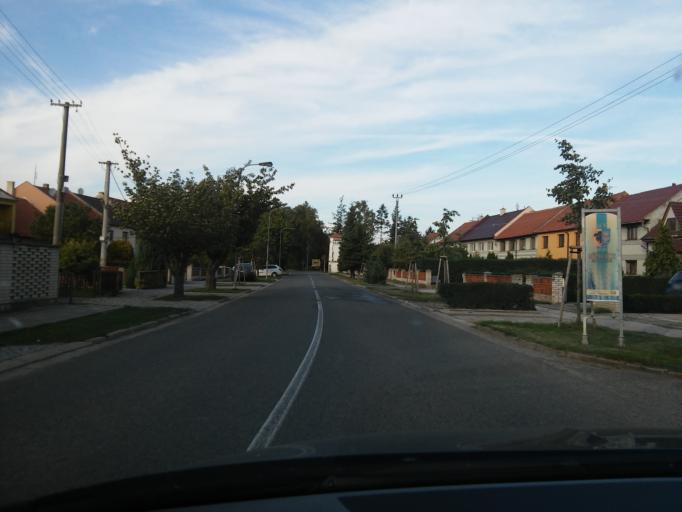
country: CZ
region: Olomoucky
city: Nemcice nad Hanou
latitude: 49.3385
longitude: 17.2010
